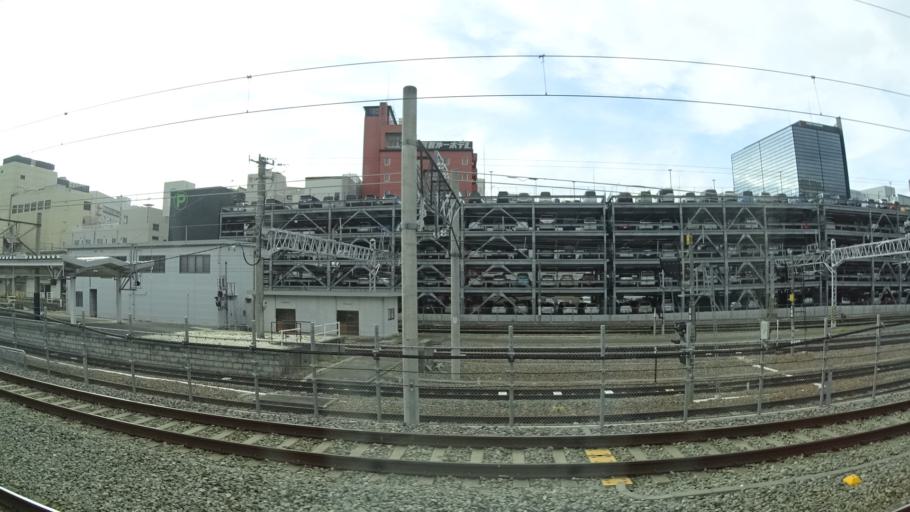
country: JP
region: Nagano
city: Nagano-shi
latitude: 36.6444
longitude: 138.1911
